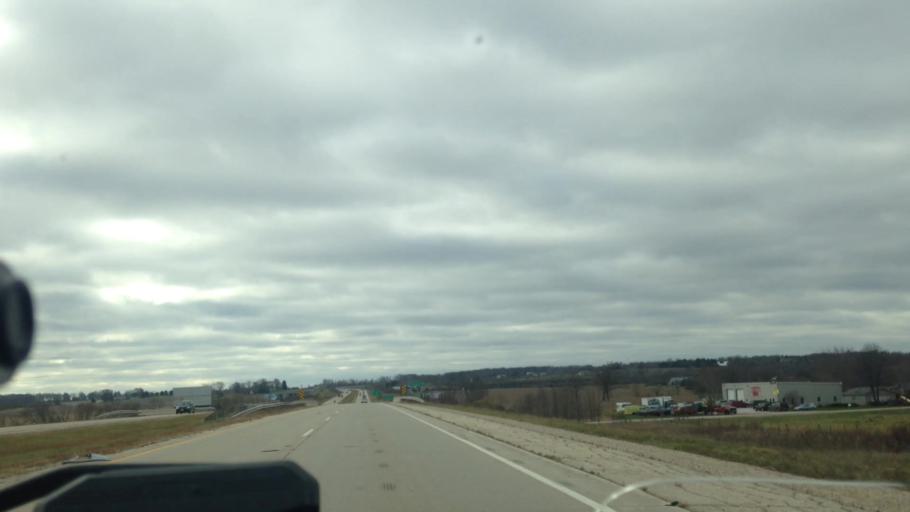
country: US
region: Wisconsin
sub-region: Washington County
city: Jackson
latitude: 43.3114
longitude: -88.1850
